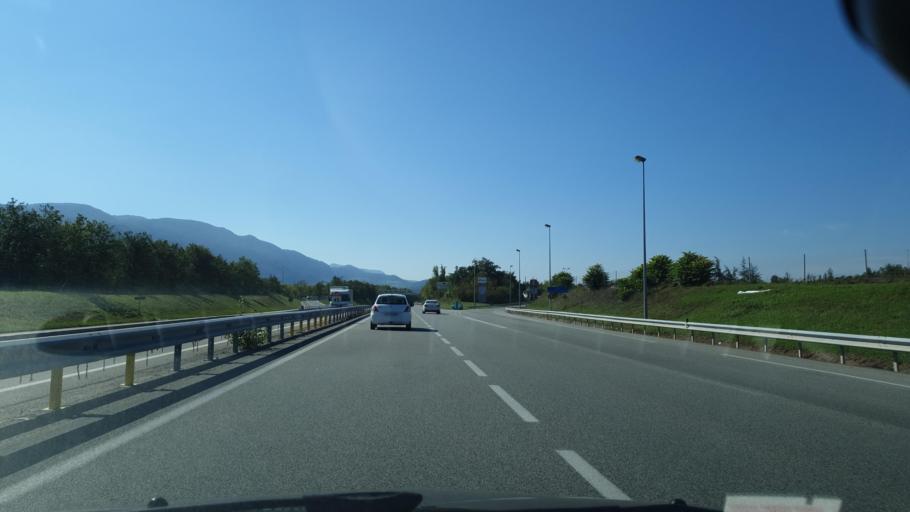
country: FR
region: Rhone-Alpes
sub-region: Departement de l'Isere
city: Saint-Lattier
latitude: 45.0783
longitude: 5.2132
